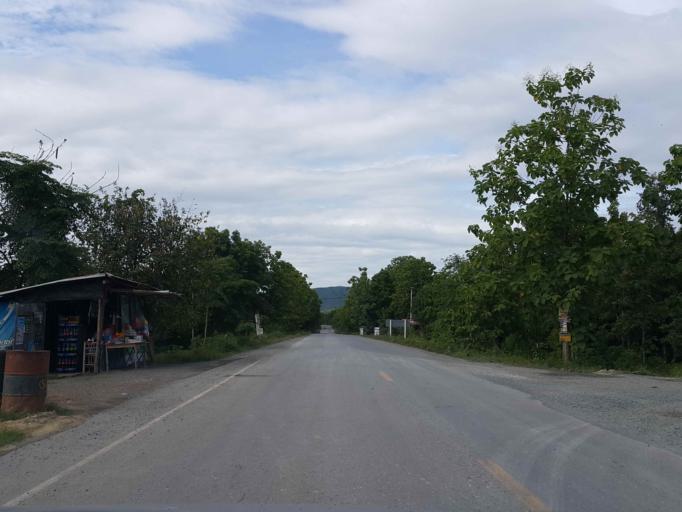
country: TH
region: Sukhothai
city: Thung Saliam
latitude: 17.2496
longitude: 99.5189
